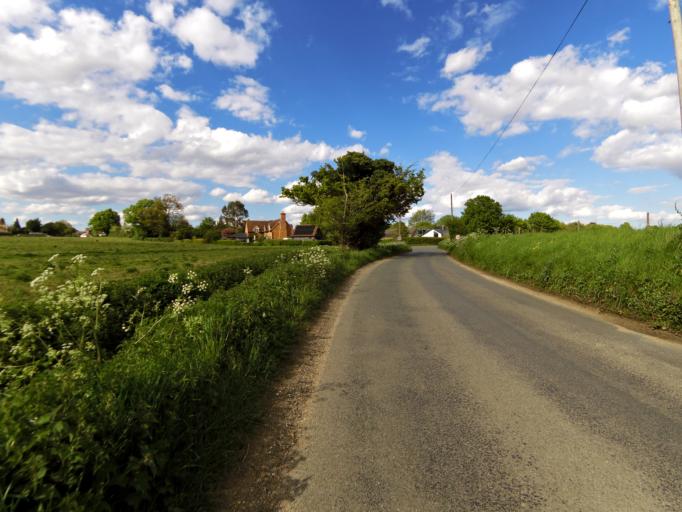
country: GB
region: England
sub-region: Suffolk
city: Woolpit
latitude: 52.2220
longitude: 0.8819
